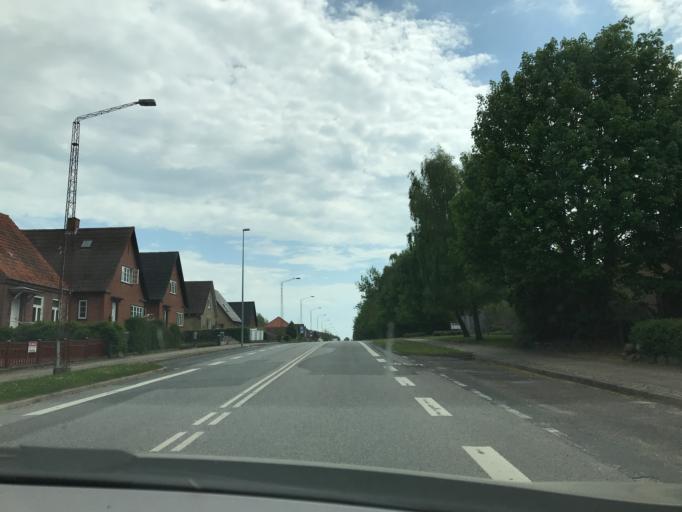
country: DK
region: South Denmark
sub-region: Assens Kommune
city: Assens
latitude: 55.2648
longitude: 9.9043
